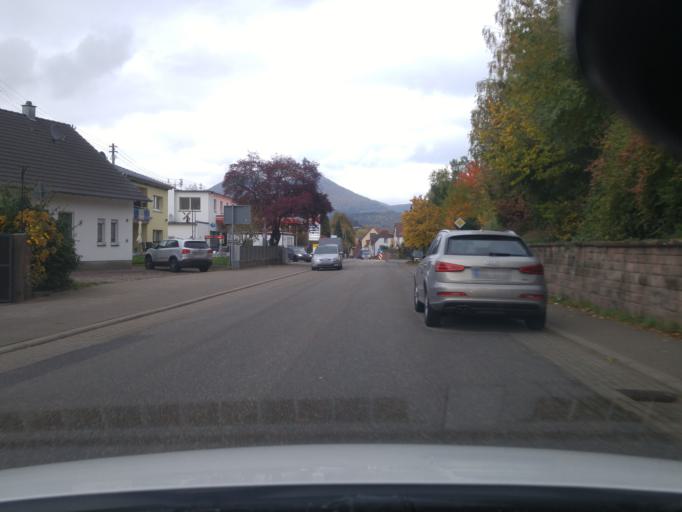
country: DE
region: Rheinland-Pfalz
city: Annweiler am Trifels
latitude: 49.2144
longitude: 7.9880
